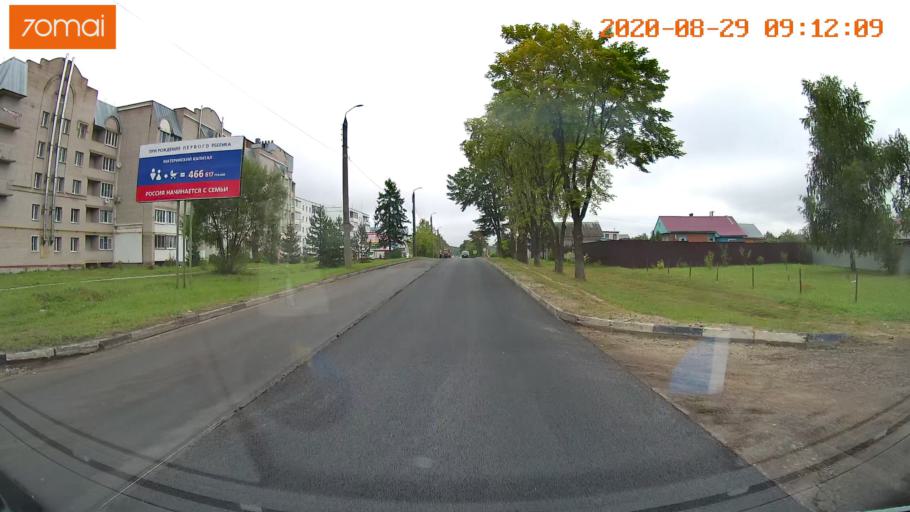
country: RU
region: Ivanovo
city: Kineshma
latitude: 57.4277
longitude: 42.0932
